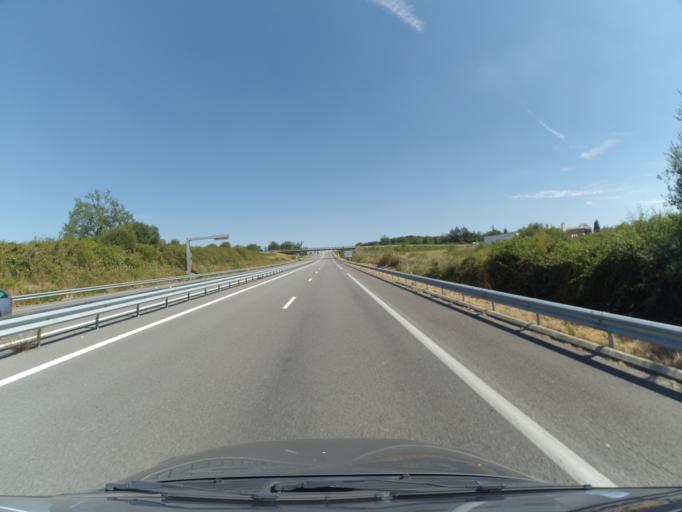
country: FR
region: Limousin
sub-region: Departement de la Haute-Vienne
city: Saint-Victurnien
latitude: 45.9021
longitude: 1.0195
